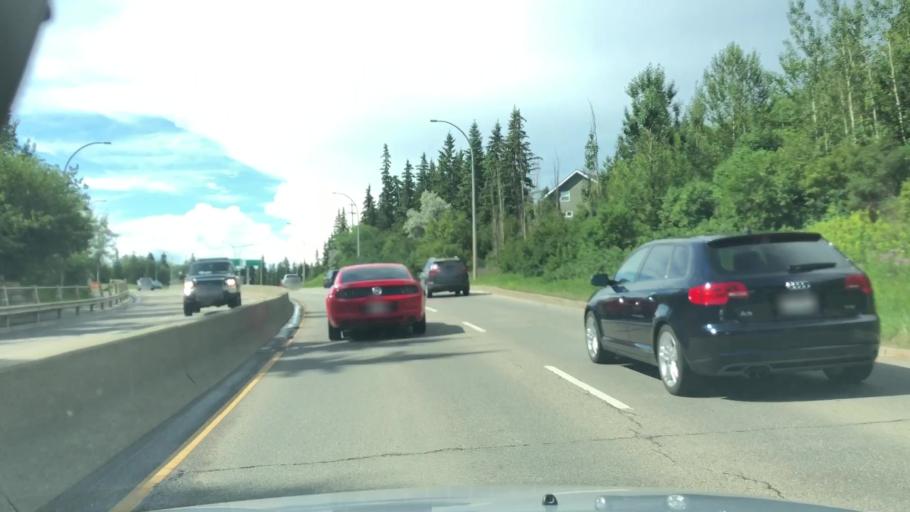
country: CA
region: Alberta
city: Edmonton
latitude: 53.5480
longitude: -113.5460
